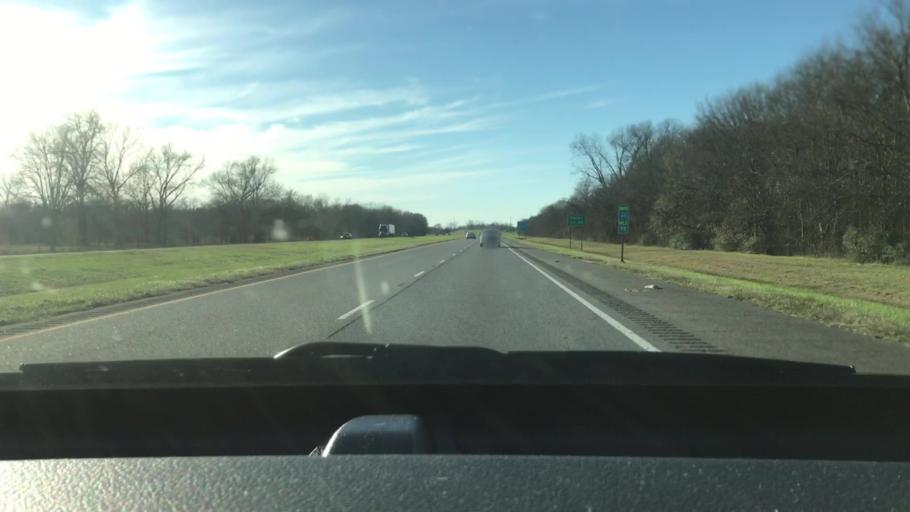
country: US
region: Louisiana
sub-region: Rapides Parish
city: Boyce
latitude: 31.3804
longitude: -92.6553
